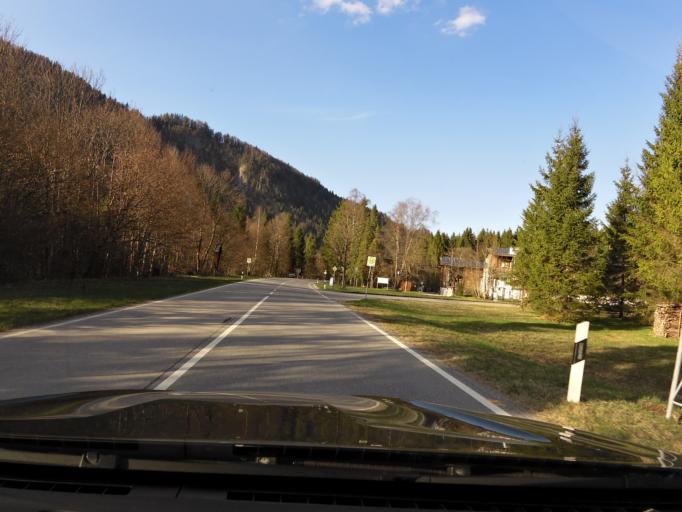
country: DE
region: Bavaria
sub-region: Upper Bavaria
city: Jachenau
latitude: 47.5698
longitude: 11.5301
